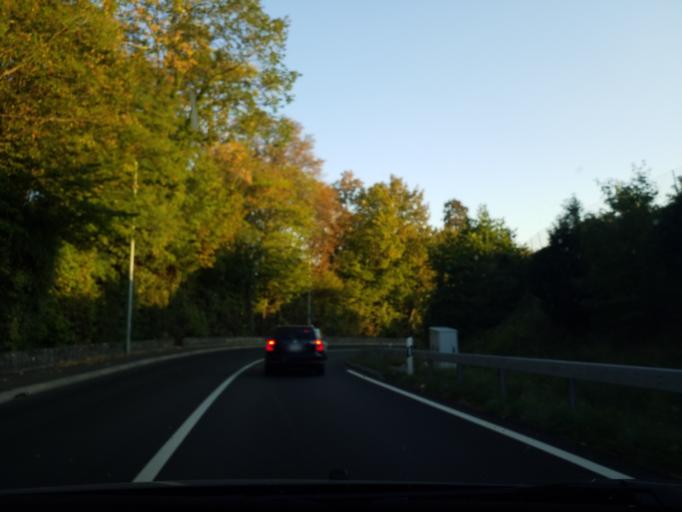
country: CH
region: Vaud
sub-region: Riviera-Pays-d'Enhaut District
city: La Tour-de-Peilz
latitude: 46.4669
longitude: 6.8660
